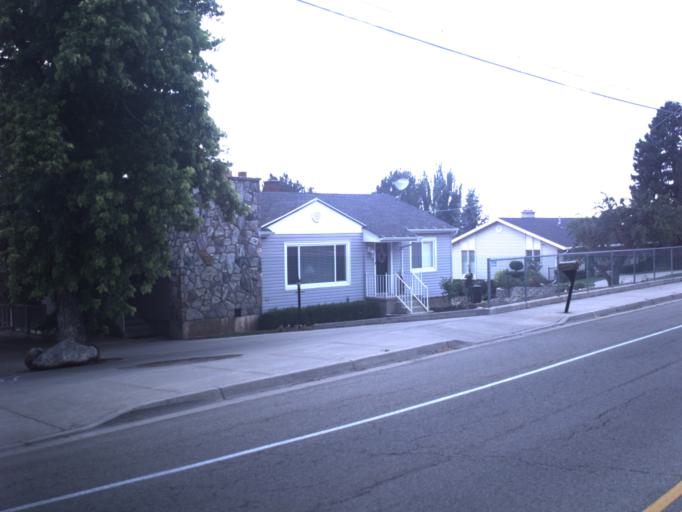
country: US
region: Utah
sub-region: Davis County
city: Centerville
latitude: 40.9475
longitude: -111.8819
